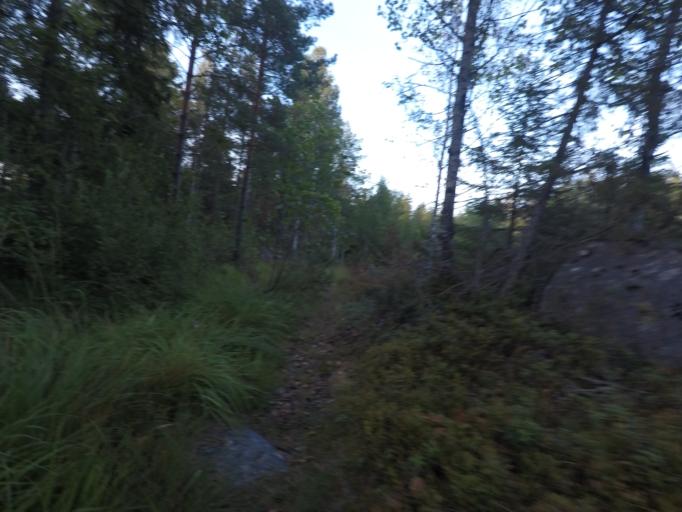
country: SE
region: Soedermanland
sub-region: Eskilstuna Kommun
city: Kvicksund
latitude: 59.4199
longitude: 16.3051
